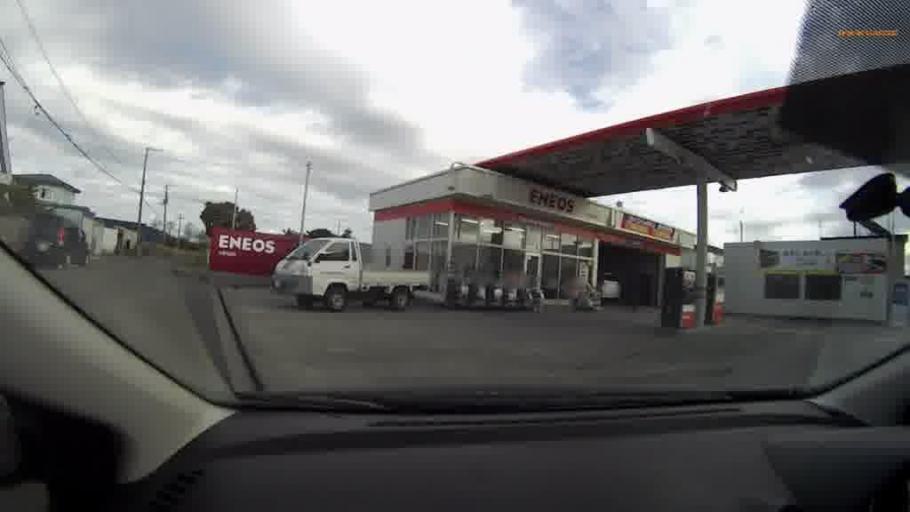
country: JP
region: Hokkaido
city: Kushiro
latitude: 43.0100
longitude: 144.2706
